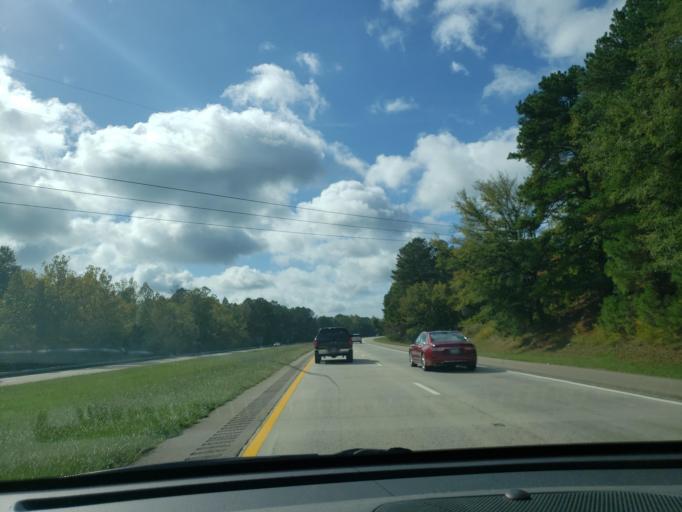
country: US
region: North Carolina
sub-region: Vance County
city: South Henderson
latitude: 36.3197
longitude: -78.4693
